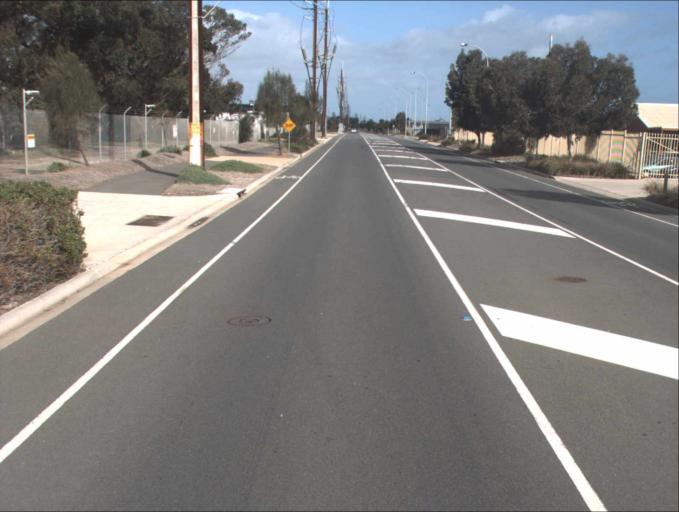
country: AU
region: South Australia
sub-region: Port Adelaide Enfield
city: Birkenhead
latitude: -34.7832
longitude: 138.5077
